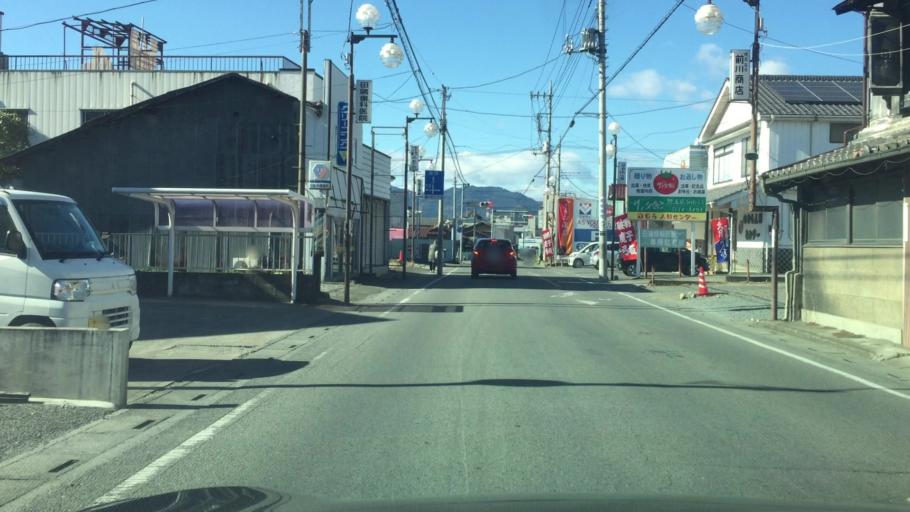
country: JP
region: Saitama
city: Kodamacho-kodamaminami
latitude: 36.1899
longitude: 139.1300
